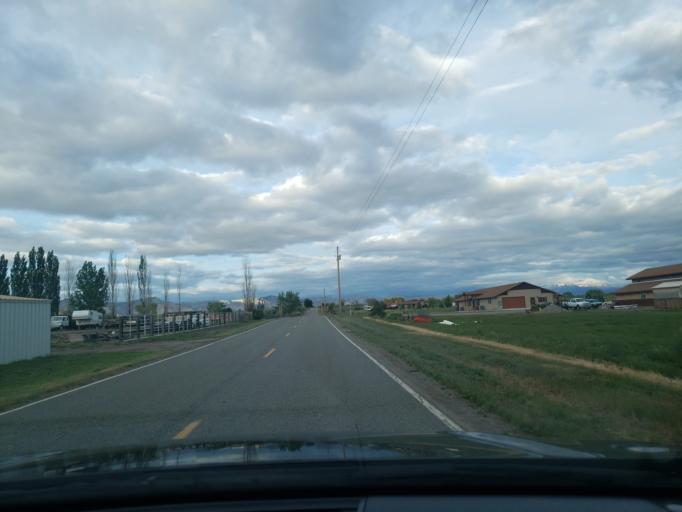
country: US
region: Colorado
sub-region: Mesa County
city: Fruita
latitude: 39.2221
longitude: -108.7168
